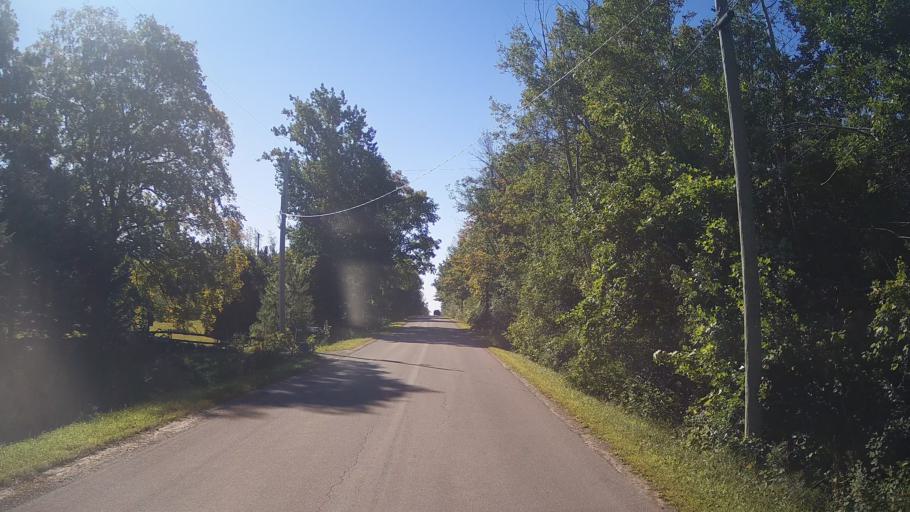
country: CA
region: Ontario
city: Prescott
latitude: 45.0059
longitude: -75.6038
